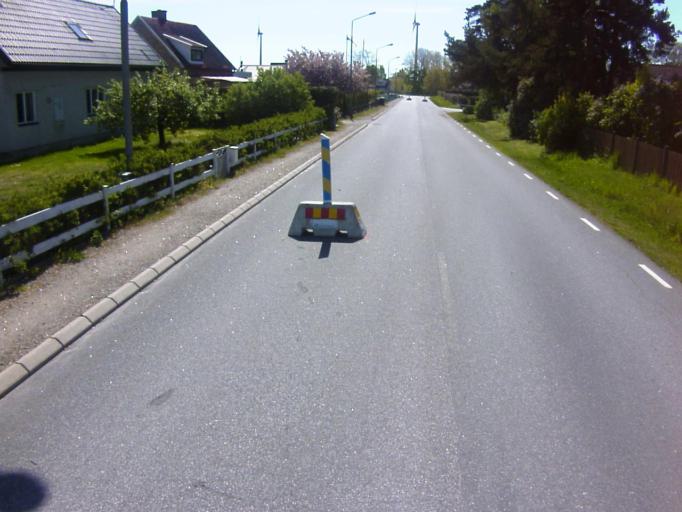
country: SE
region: Blekinge
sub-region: Solvesborgs Kommun
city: Soelvesborg
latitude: 56.0563
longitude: 14.6244
